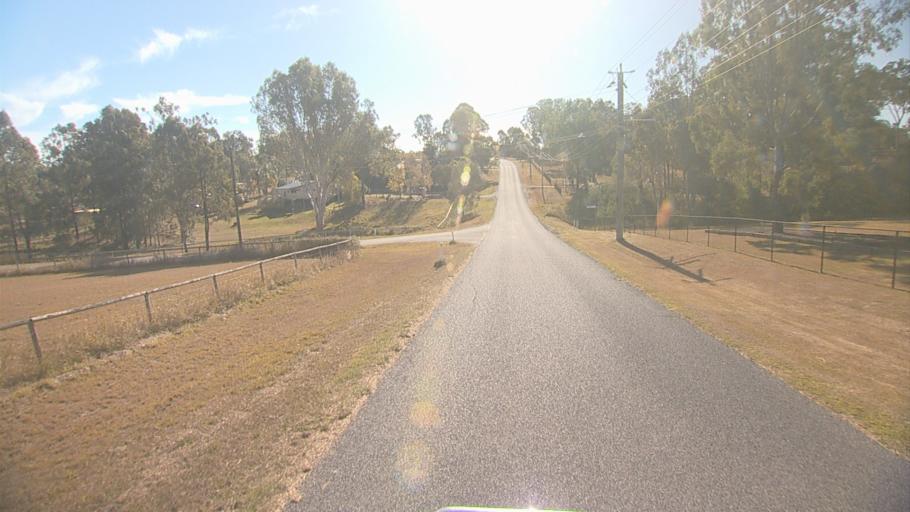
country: AU
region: Queensland
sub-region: Logan
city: Cedar Vale
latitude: -27.8680
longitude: 152.9836
